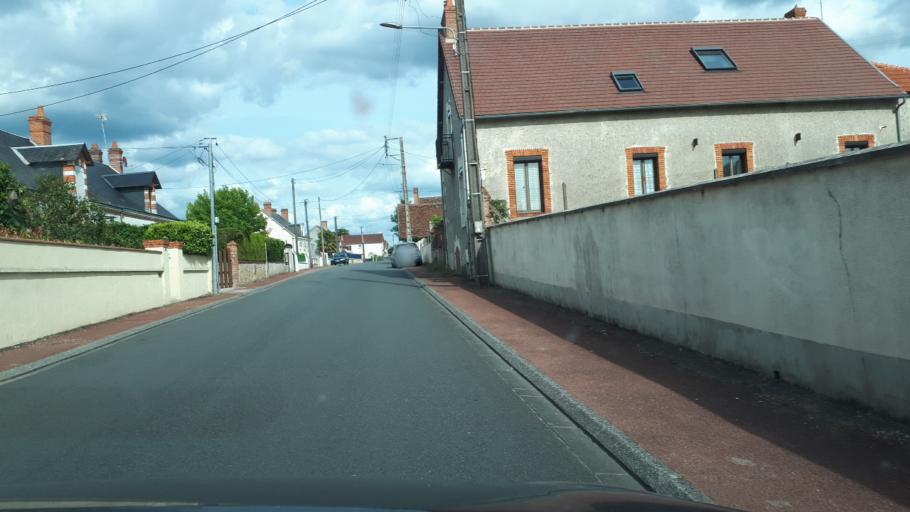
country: FR
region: Centre
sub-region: Departement du Loir-et-Cher
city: Romorantin-Lanthenay
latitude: 47.3529
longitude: 1.7523
